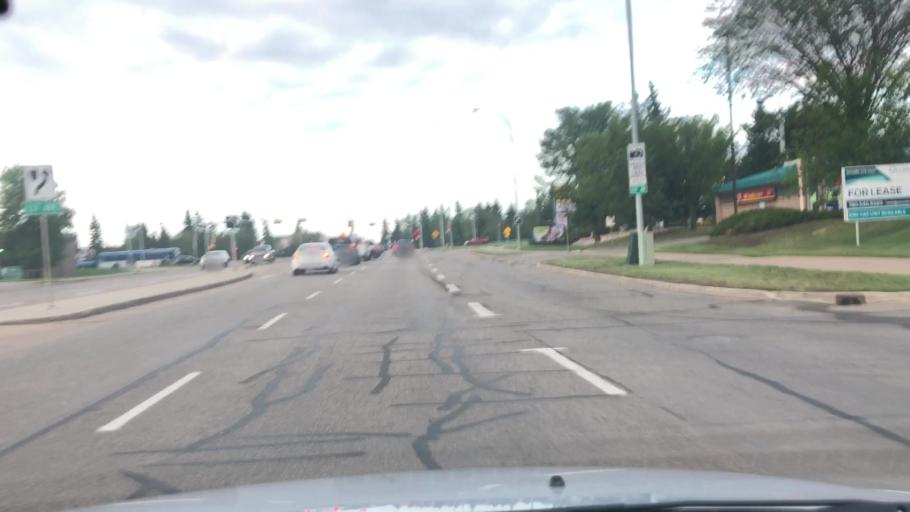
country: CA
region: Alberta
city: Edmonton
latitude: 53.6008
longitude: -113.5413
